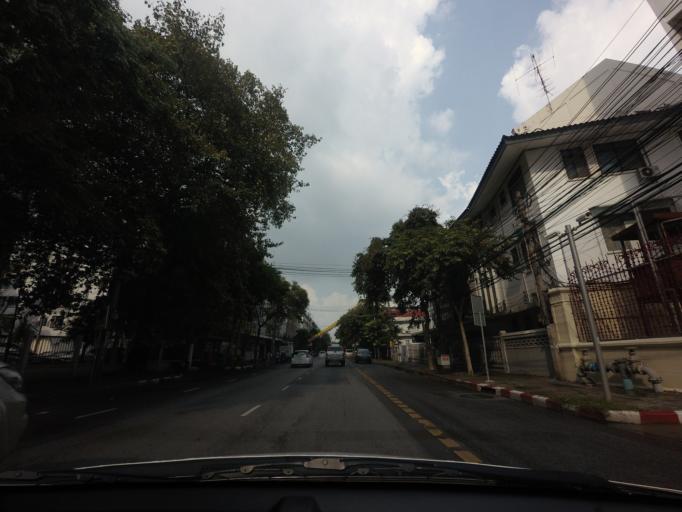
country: TH
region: Bangkok
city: Phra Nakhon
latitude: 13.7640
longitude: 100.5053
